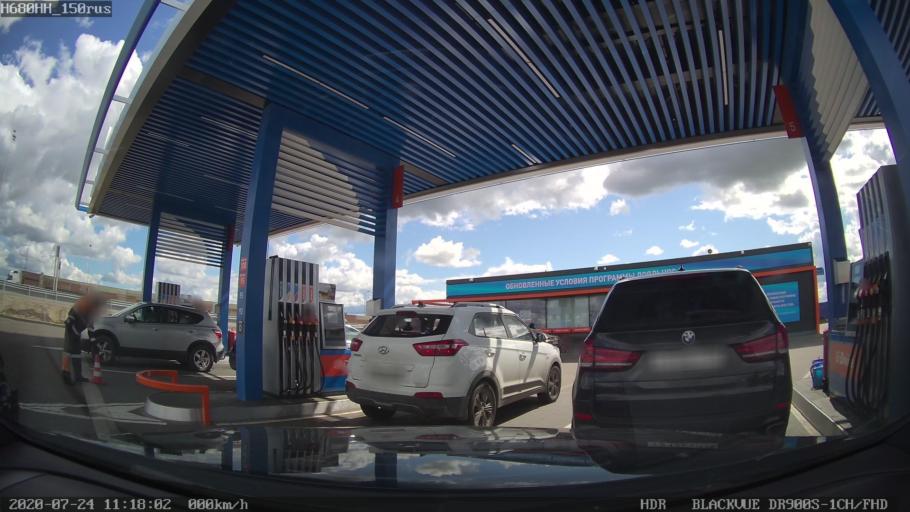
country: RU
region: Leningrad
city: Fedorovskoye
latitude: 59.7010
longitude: 30.5529
